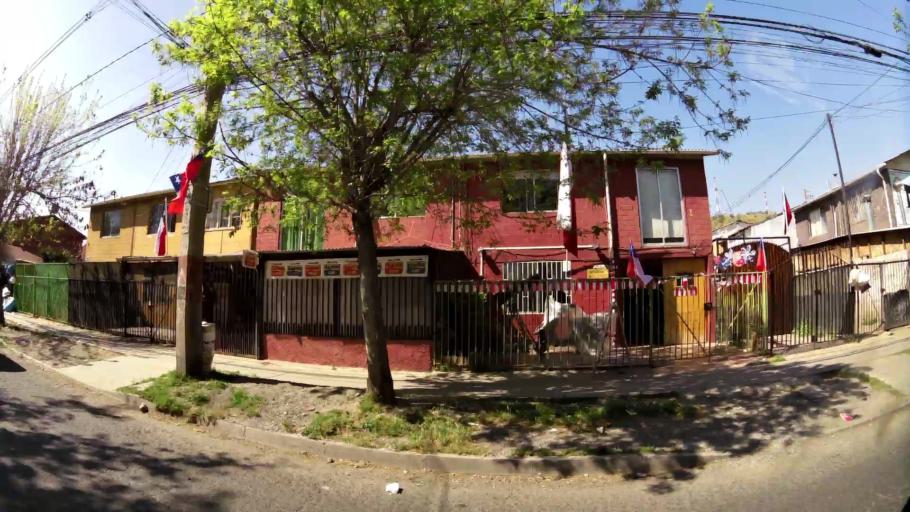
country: CL
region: Santiago Metropolitan
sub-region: Provincia de Cordillera
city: Puente Alto
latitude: -33.6239
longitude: -70.6077
